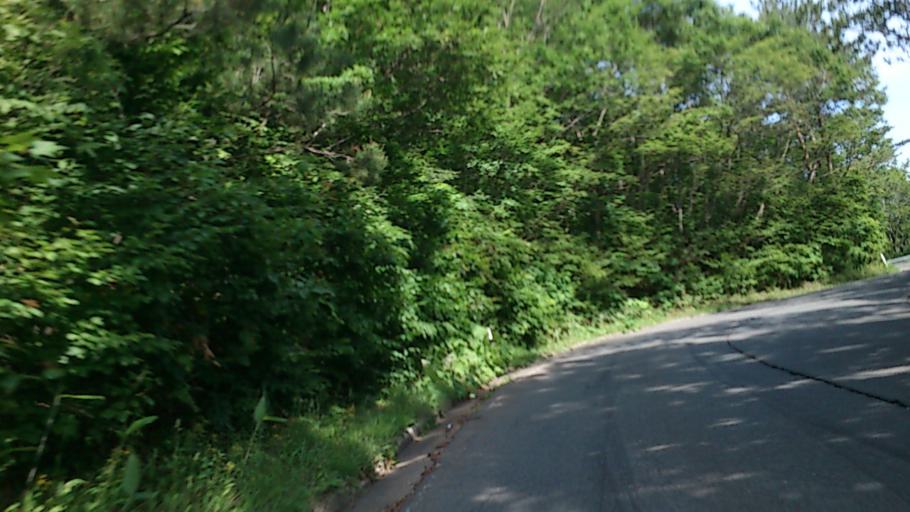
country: JP
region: Aomori
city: Aomori Shi
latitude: 40.7144
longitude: 140.8212
